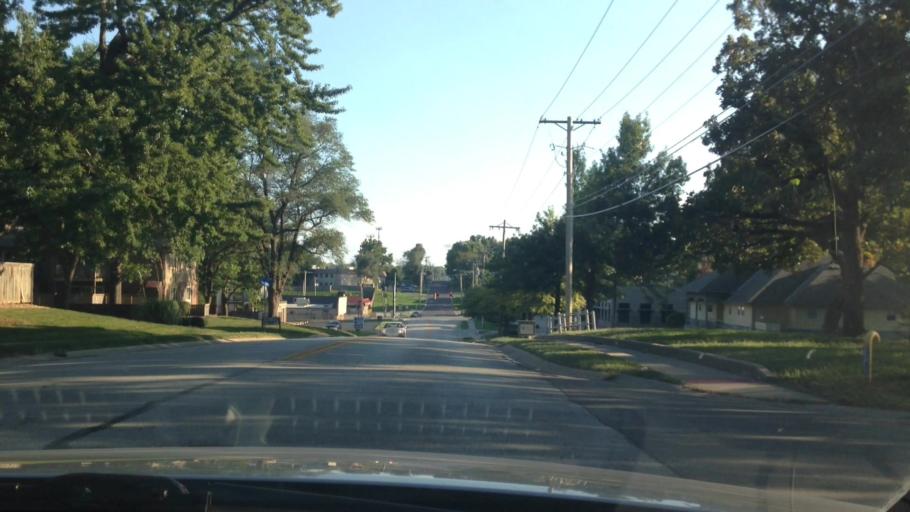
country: US
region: Kansas
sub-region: Johnson County
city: Merriam
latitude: 38.9952
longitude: -94.7050
